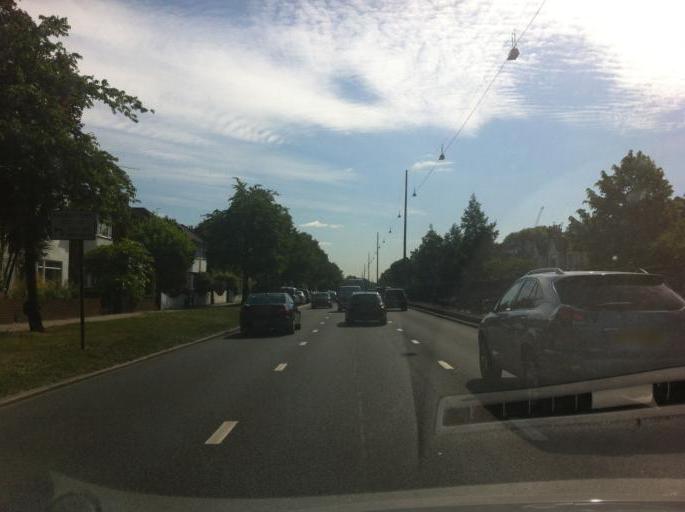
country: GB
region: England
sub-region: Greater London
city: Acton
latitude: 51.4885
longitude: -0.2738
